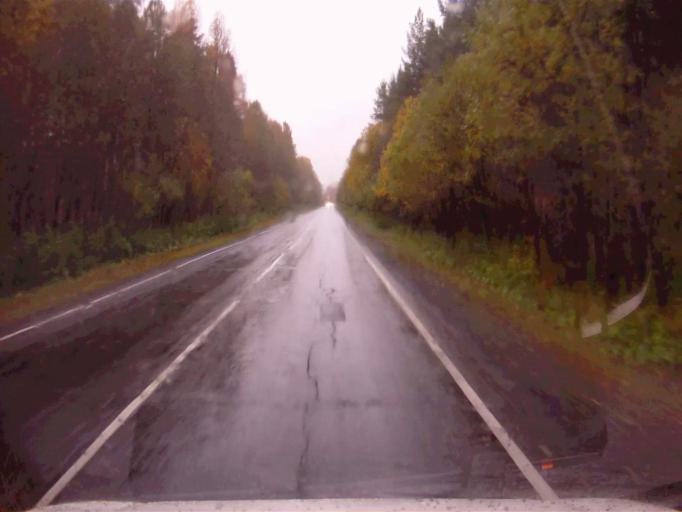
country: RU
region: Chelyabinsk
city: Verkhniy Ufaley
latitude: 55.9379
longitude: 60.4126
